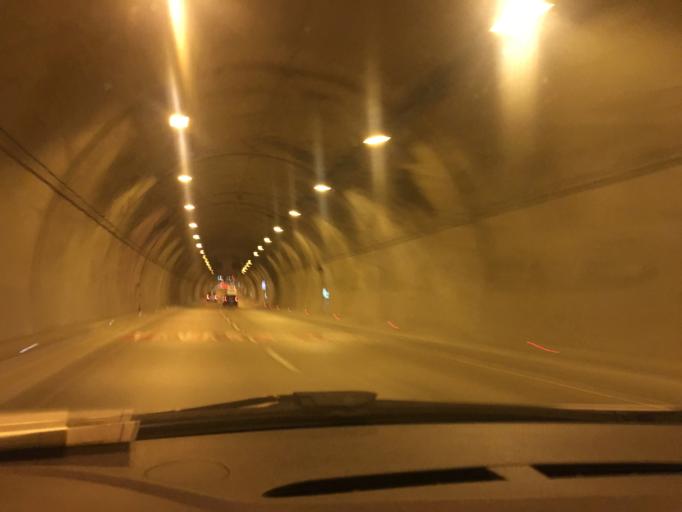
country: TR
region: Istanbul
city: Sisli
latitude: 41.0581
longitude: 28.9766
